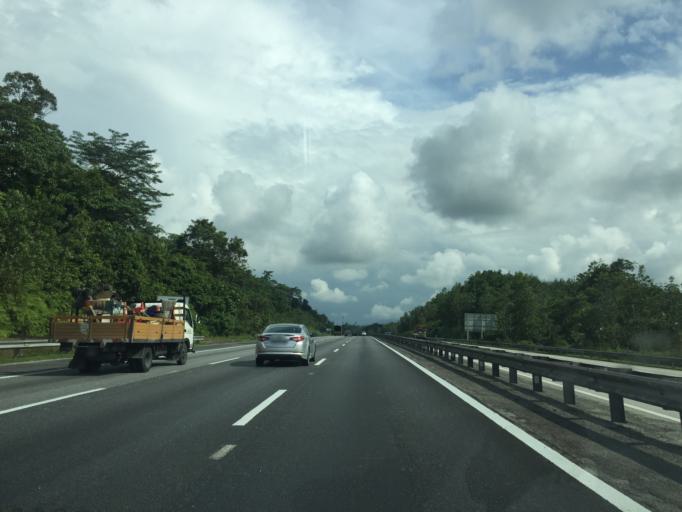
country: MY
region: Selangor
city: Batang Berjuntai
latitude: 3.5586
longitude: 101.5196
